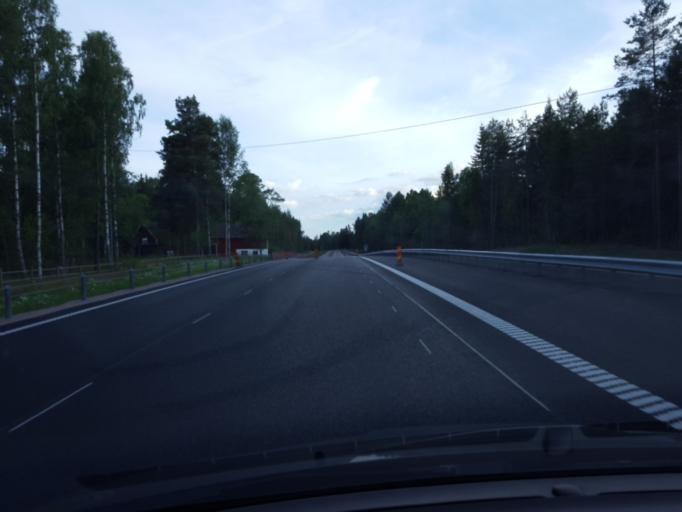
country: SE
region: Uppsala
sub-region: Osthammars Kommun
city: Gimo
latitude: 60.1124
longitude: 18.1301
